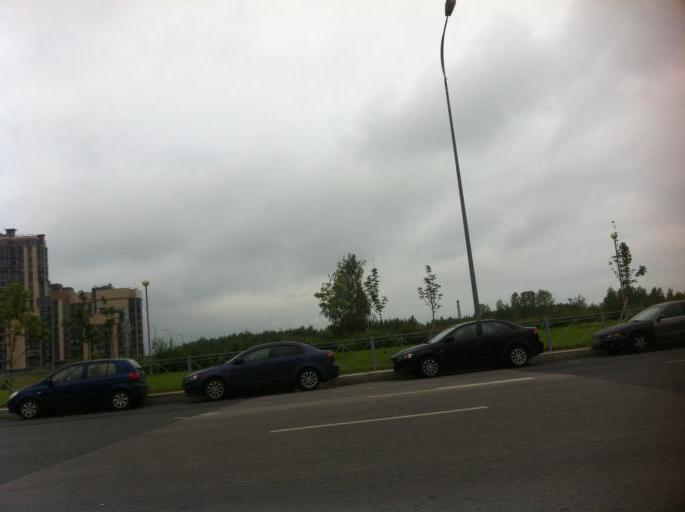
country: RU
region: St.-Petersburg
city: Sosnovaya Polyana
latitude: 59.8548
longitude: 30.1474
